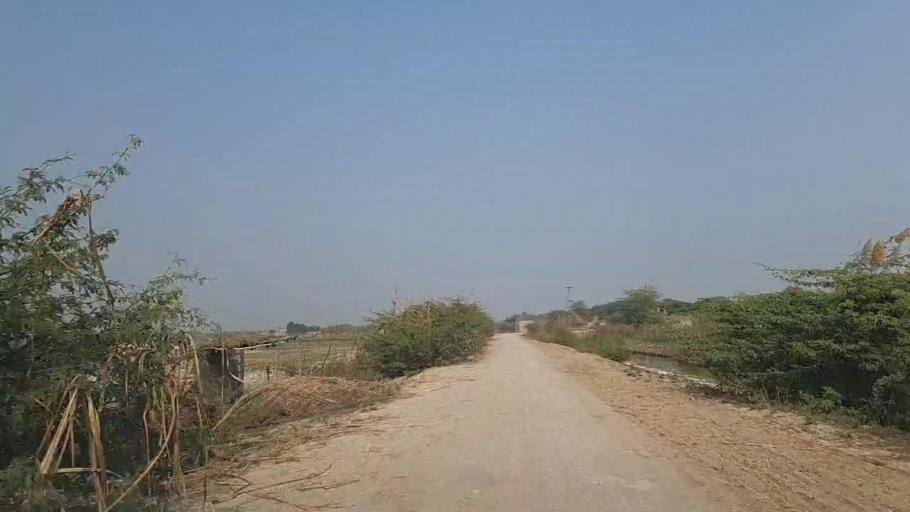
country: PK
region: Sindh
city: Daur
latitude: 26.4372
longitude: 68.4426
